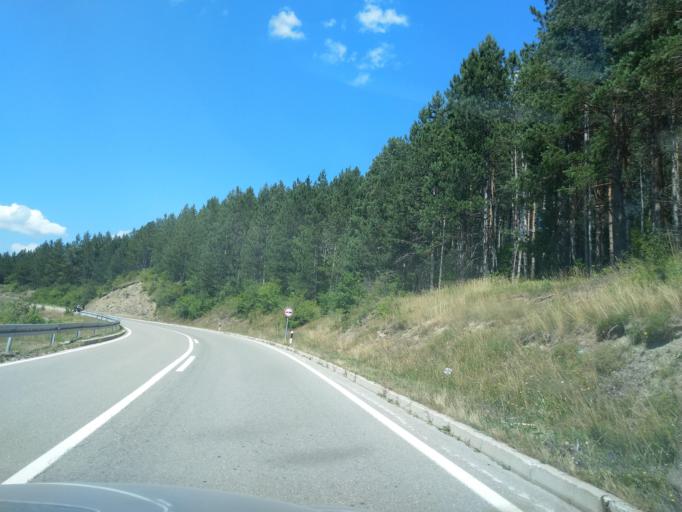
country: RS
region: Central Serbia
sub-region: Zlatiborski Okrug
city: Sjenica
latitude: 43.3050
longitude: 19.9297
